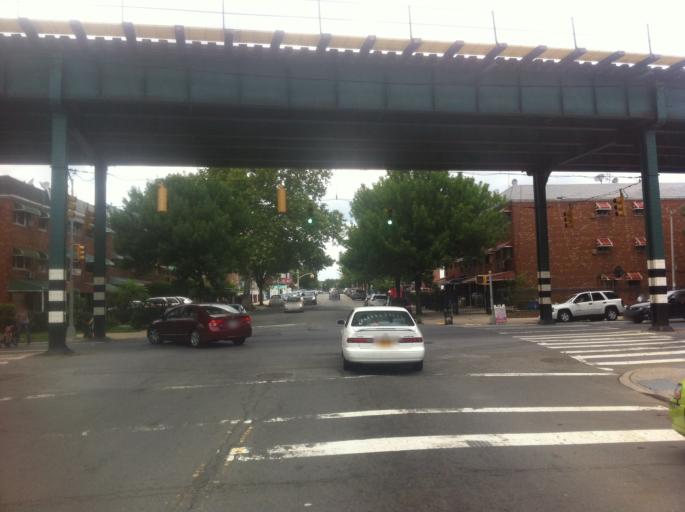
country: US
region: New York
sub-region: Bronx
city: The Bronx
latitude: 40.8309
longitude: -73.8690
